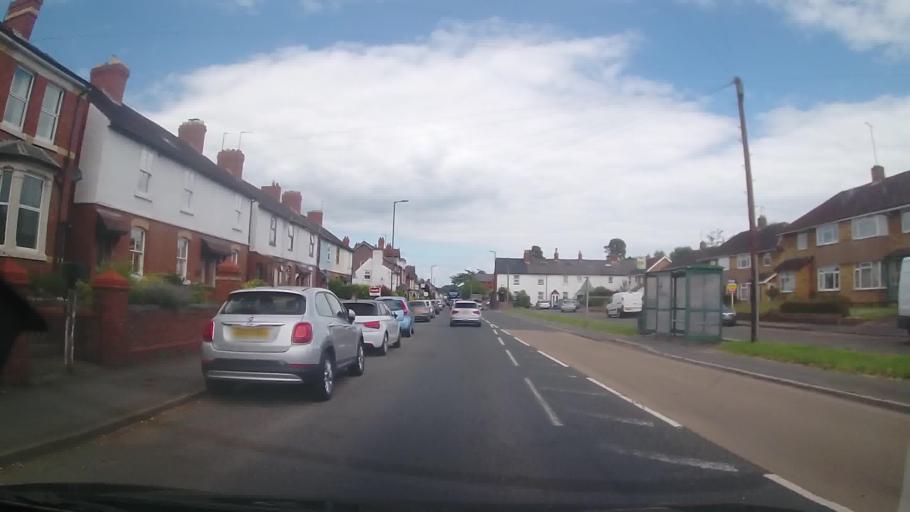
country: GB
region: England
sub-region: Herefordshire
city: Belmont
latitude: 52.0460
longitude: -2.7267
